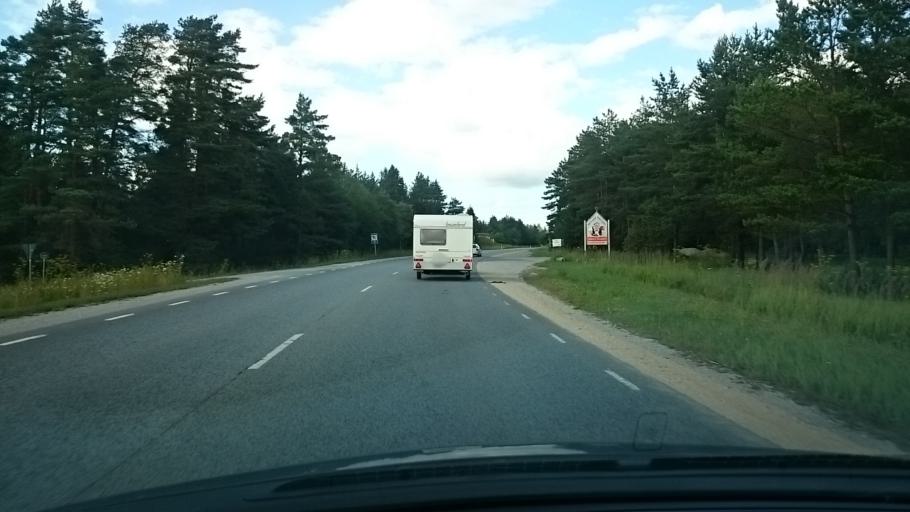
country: EE
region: Harju
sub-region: Keila linn
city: Keila
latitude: 59.2675
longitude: 24.2919
